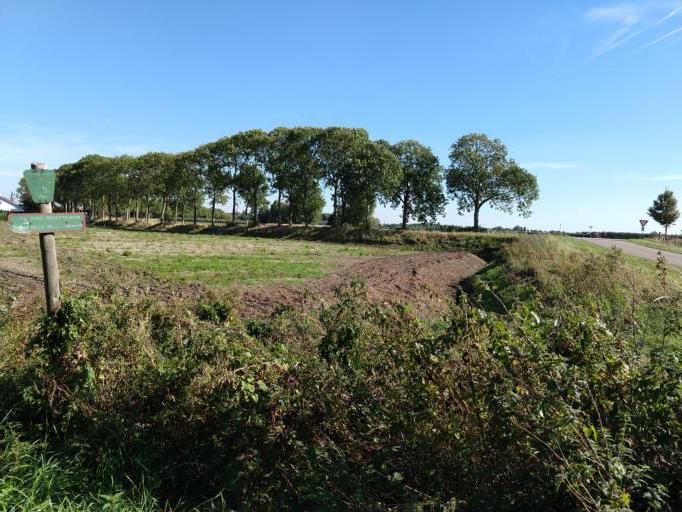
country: NL
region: Zeeland
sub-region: Gemeente Terneuzen
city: Terneuzen
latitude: 51.4070
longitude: 3.8408
